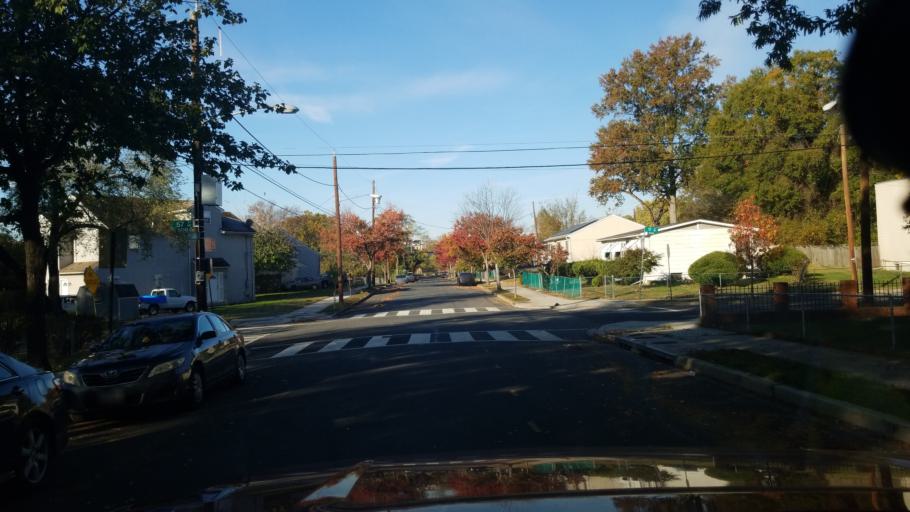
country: US
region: Maryland
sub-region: Prince George's County
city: Fairmount Heights
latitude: 38.8972
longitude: -76.9188
